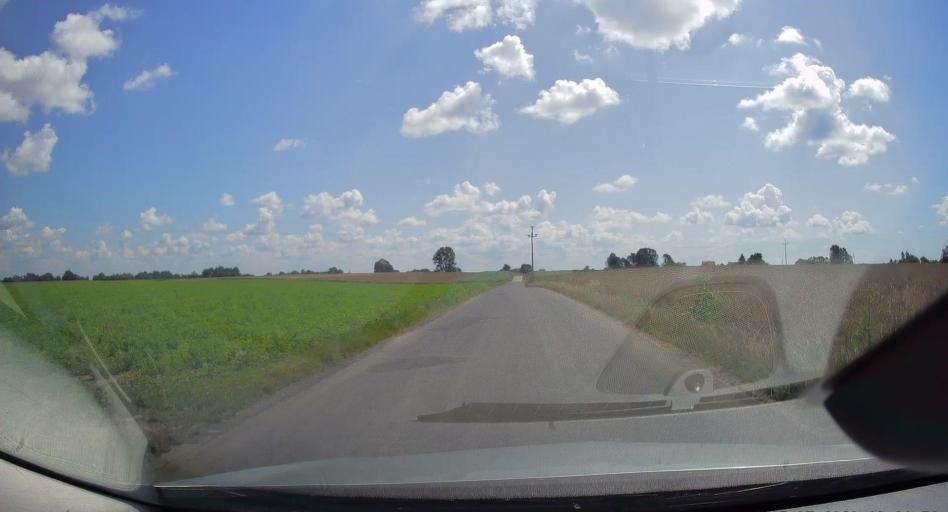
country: PL
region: Subcarpathian Voivodeship
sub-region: Powiat jaroslawski
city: Sosnica
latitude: 49.8493
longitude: 22.8803
